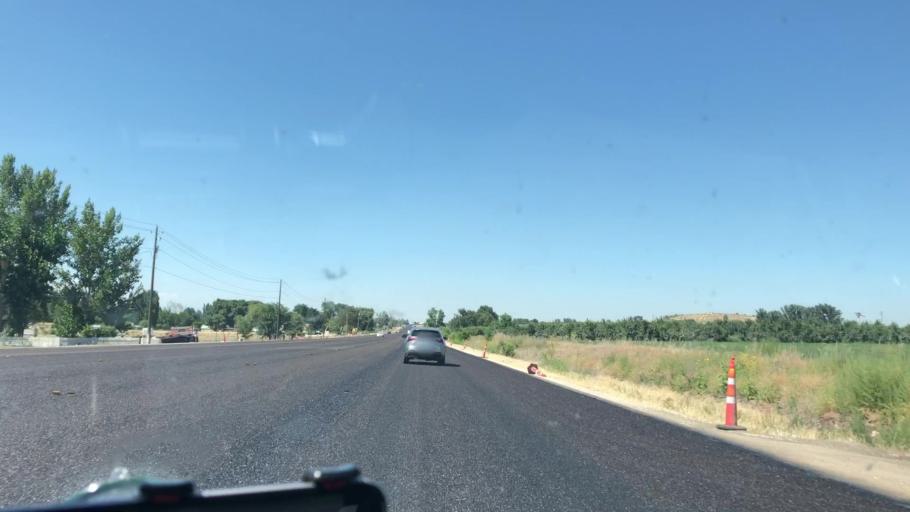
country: US
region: Idaho
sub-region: Owyhee County
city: Marsing
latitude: 43.5825
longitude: -116.7921
